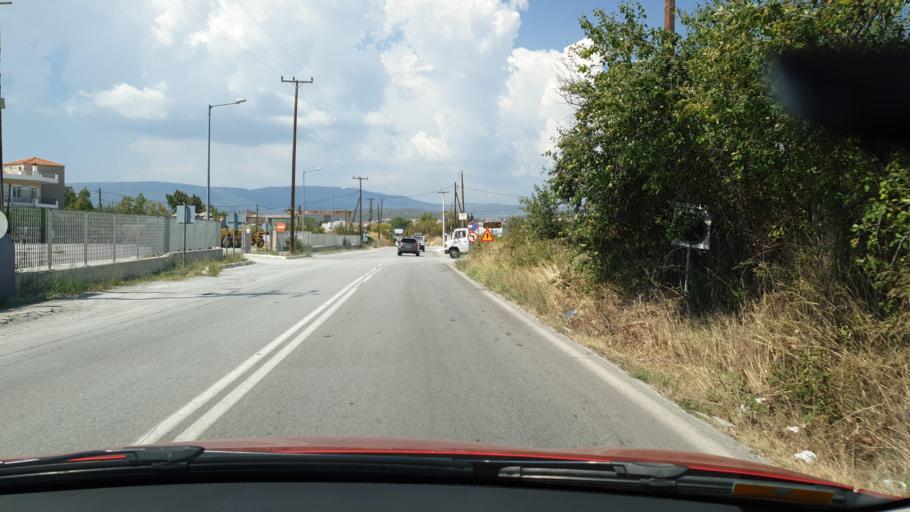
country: GR
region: Central Greece
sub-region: Nomos Evvoias
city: Aliveri
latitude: 38.3989
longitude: 24.0614
